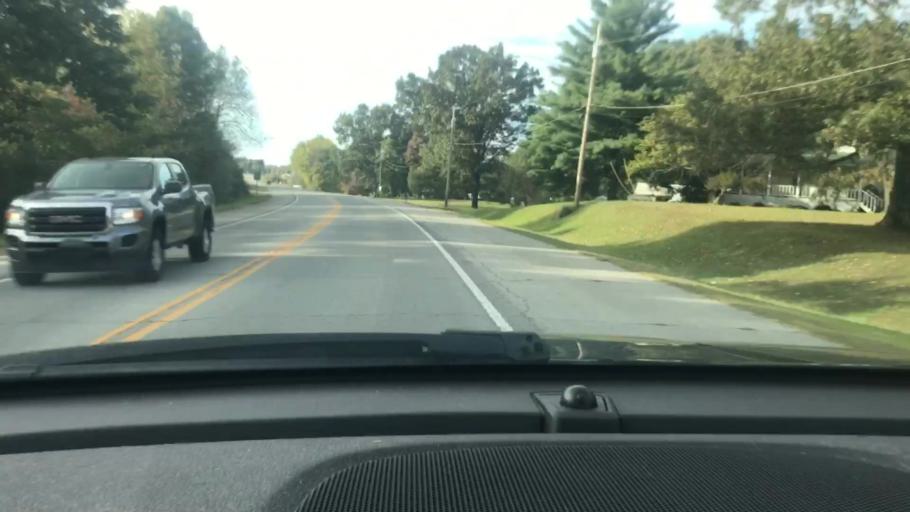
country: US
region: Tennessee
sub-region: Dickson County
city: White Bluff
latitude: 36.1277
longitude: -87.2284
